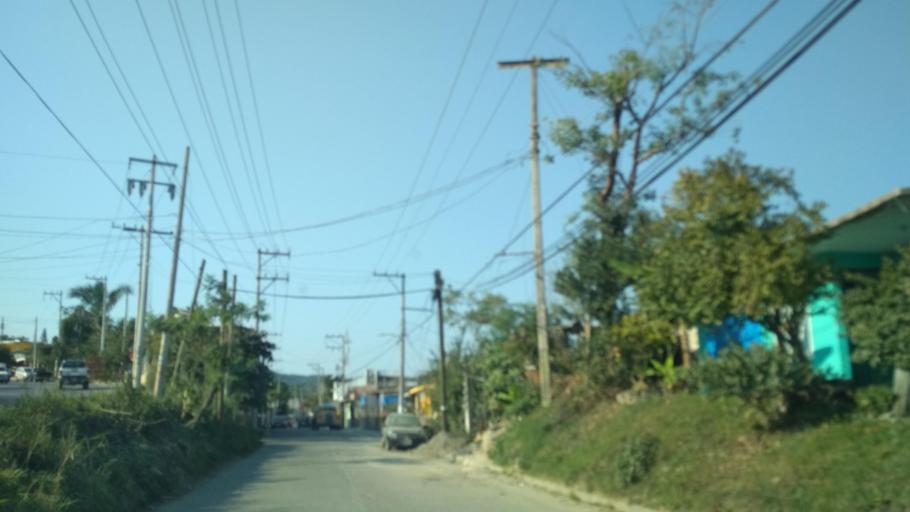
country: MM
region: Shan
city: Taunggyi
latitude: 20.4010
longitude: 97.3363
